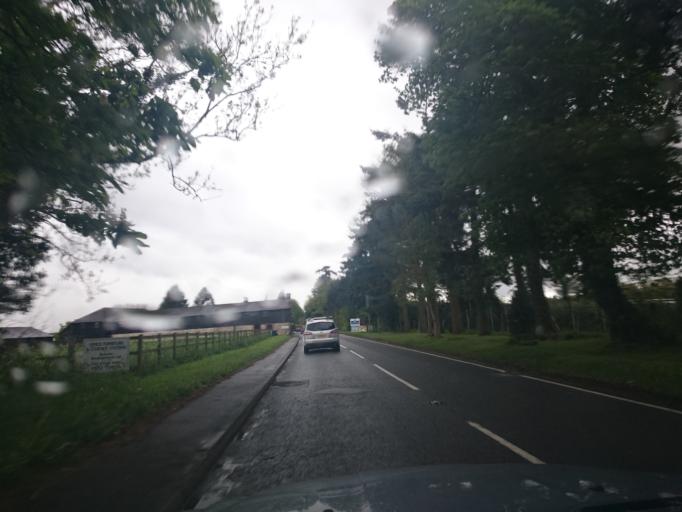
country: GB
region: England
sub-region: Surrey
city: Farnham
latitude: 51.1915
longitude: -0.8262
